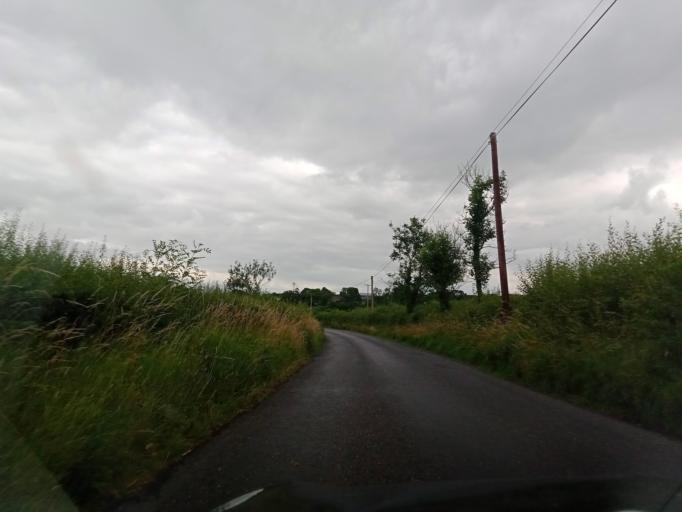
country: IE
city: Ballylinan
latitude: 52.8985
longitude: -7.1145
